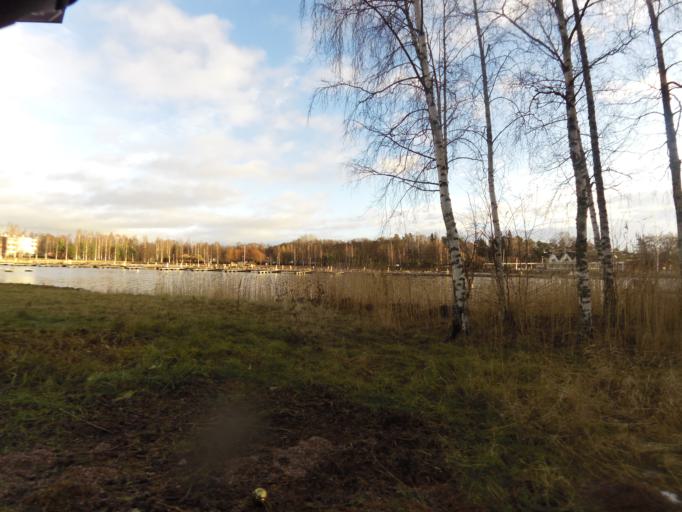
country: FI
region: Uusimaa
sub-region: Helsinki
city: Koukkuniemi
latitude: 60.1560
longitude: 24.7690
